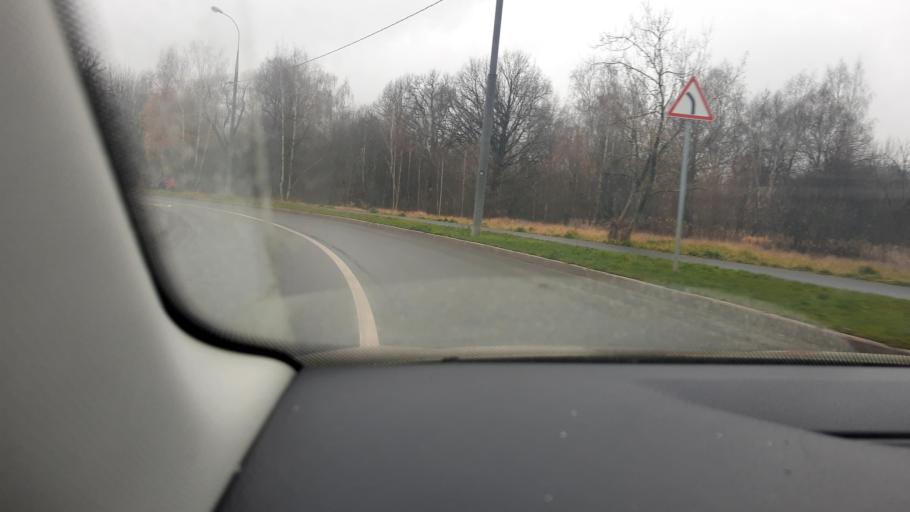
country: RU
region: Moscow
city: Annino
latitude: 55.5527
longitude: 37.5707
